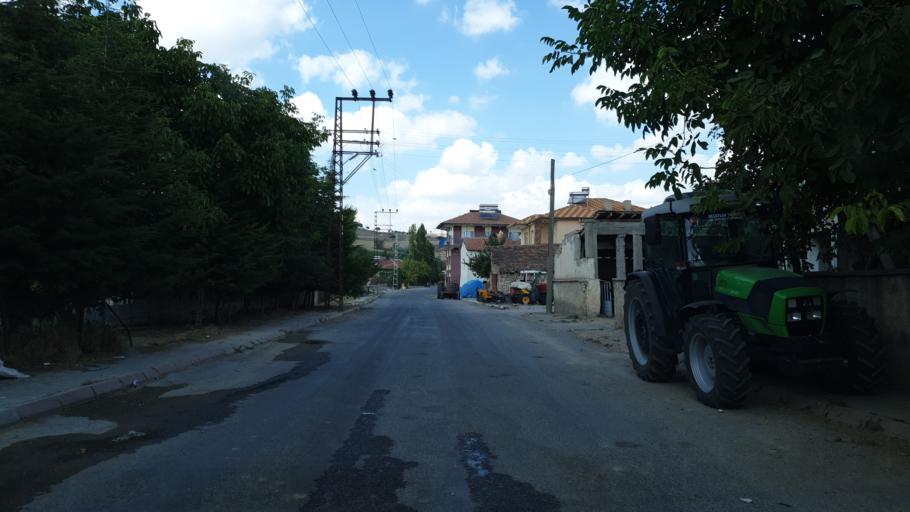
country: TR
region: Kayseri
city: Felahiye
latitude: 39.0917
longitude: 35.5632
